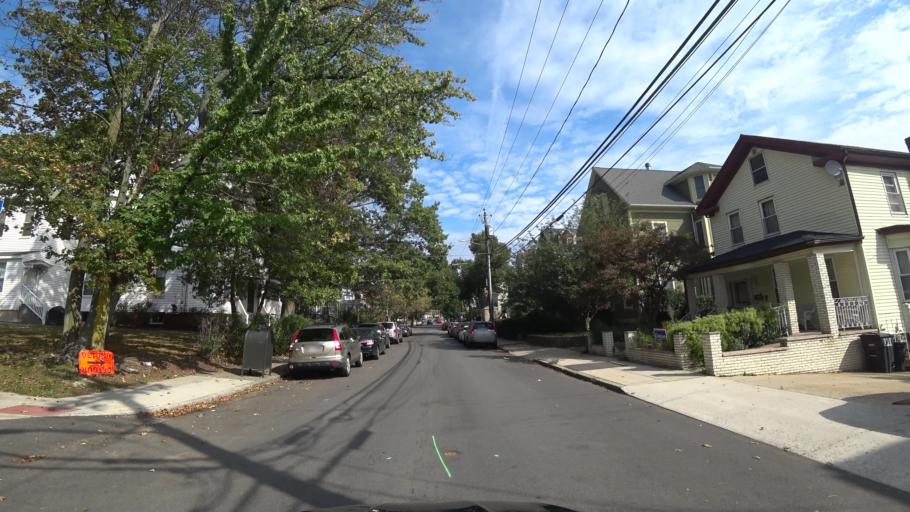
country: US
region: Massachusetts
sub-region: Middlesex County
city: Somerville
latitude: 42.3924
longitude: -71.0986
